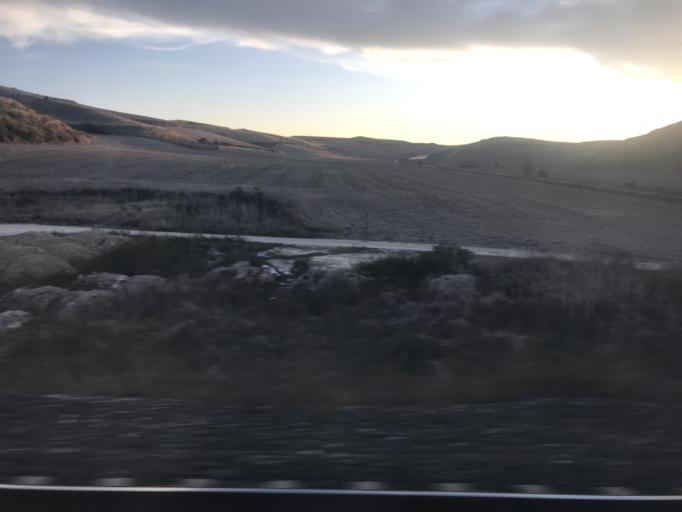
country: ES
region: Castille and Leon
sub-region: Provincia de Burgos
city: Santa Maria del Invierno
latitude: 42.4389
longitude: -3.4421
